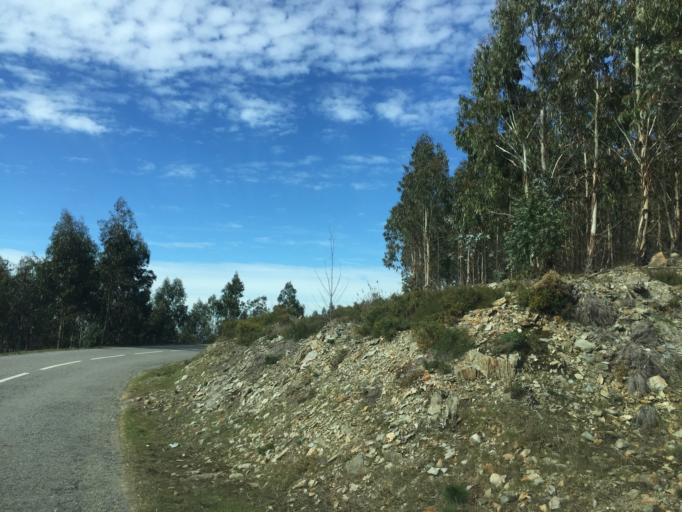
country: PT
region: Aveiro
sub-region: Arouca
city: Arouca
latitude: 40.9625
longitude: -8.2395
